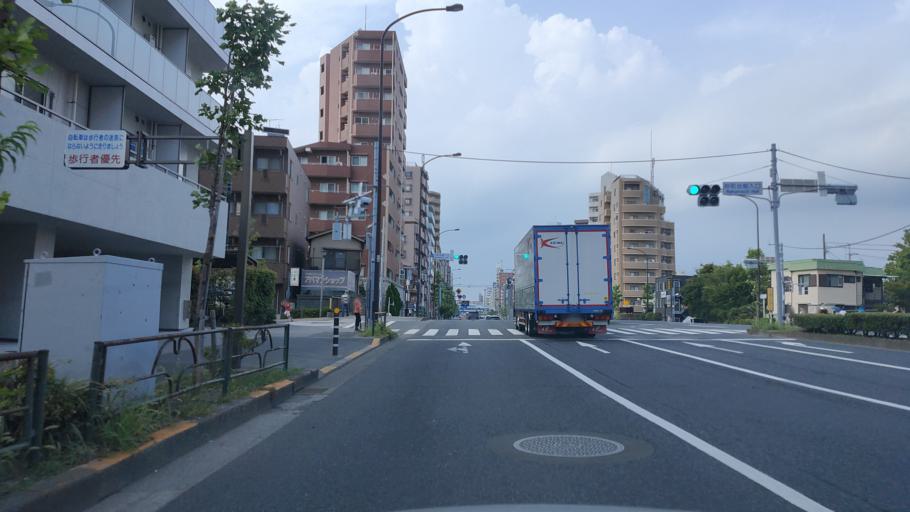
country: JP
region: Tokyo
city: Urayasu
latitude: 35.6554
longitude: 139.8725
